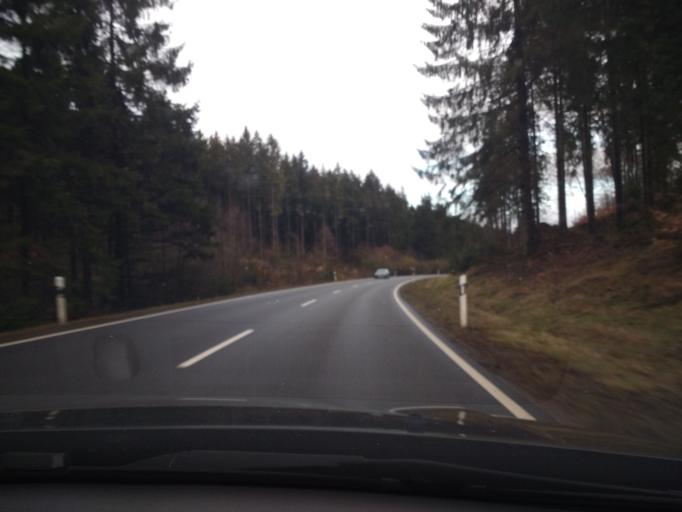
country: DE
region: Rheinland-Pfalz
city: Reinsfeld
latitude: 49.6598
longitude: 6.8580
